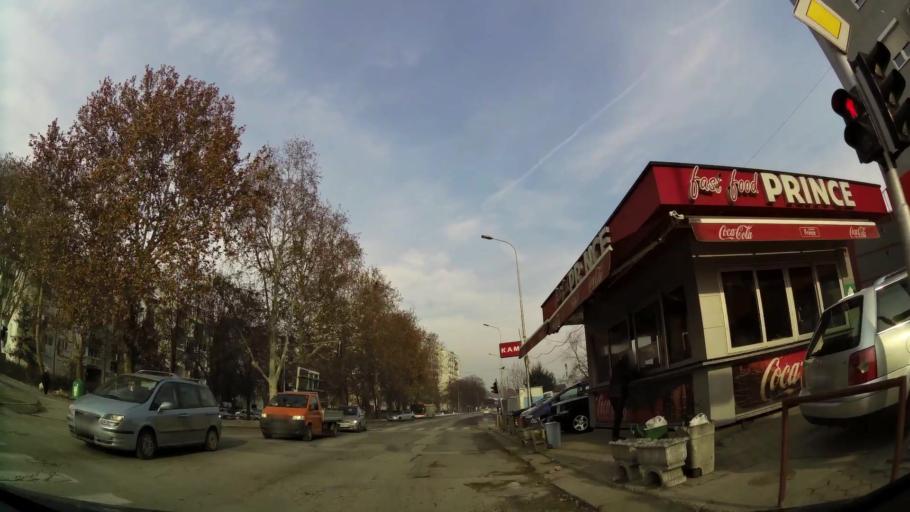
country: MK
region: Cair
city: Cair
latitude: 42.0201
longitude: 21.4346
